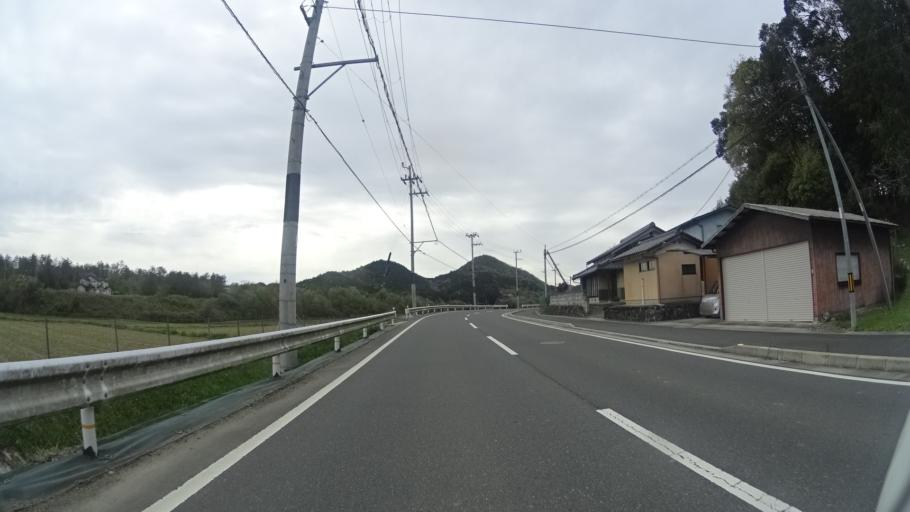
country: JP
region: Kyoto
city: Ayabe
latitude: 35.1783
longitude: 135.4420
